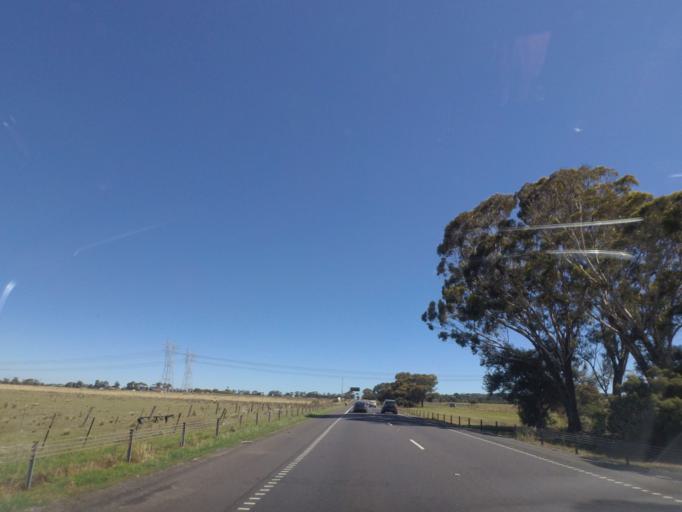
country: AU
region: Victoria
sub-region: Hume
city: Craigieburn
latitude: -37.5522
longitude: 144.9437
